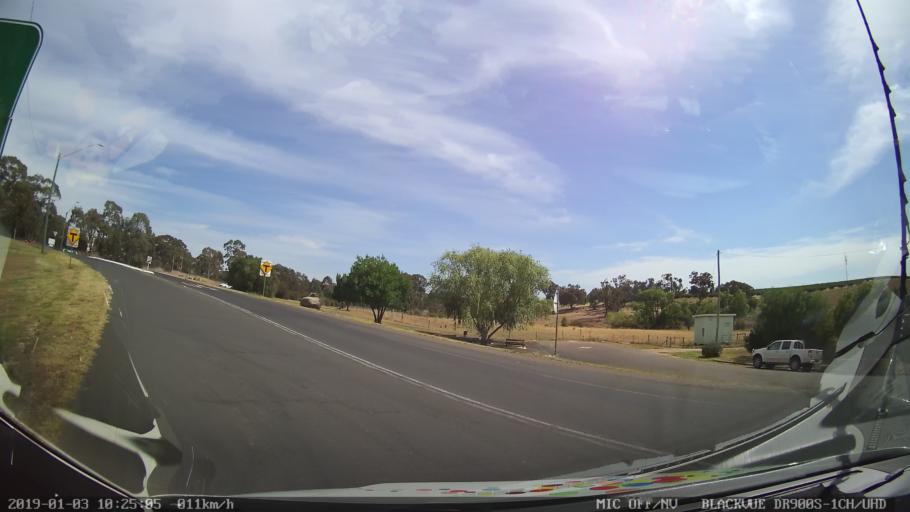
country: AU
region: New South Wales
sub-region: Young
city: Young
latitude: -34.4233
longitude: 148.2442
